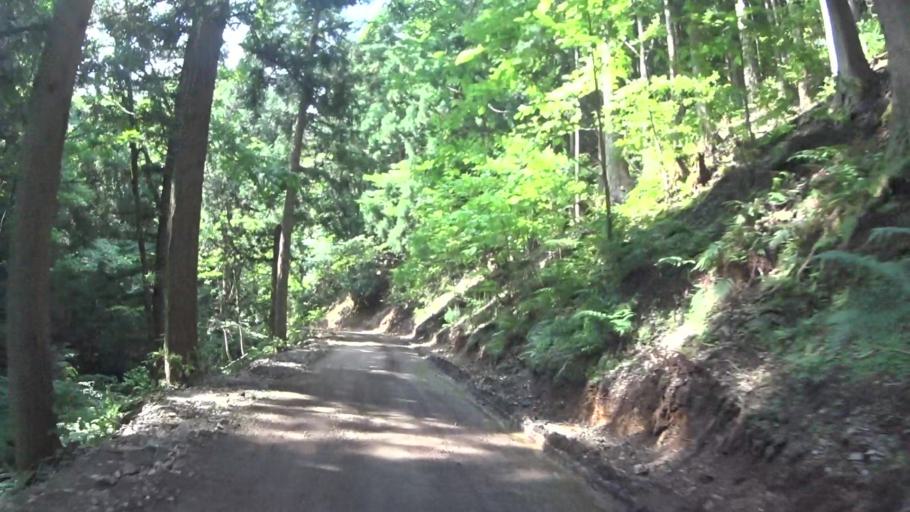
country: JP
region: Fukui
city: Obama
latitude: 35.2628
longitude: 135.6417
